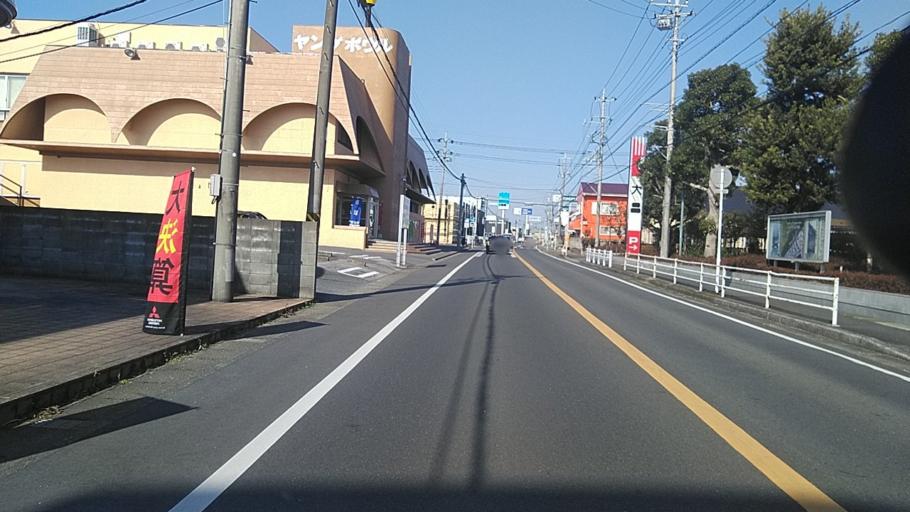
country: JP
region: Chiba
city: Mobara
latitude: 35.4345
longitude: 140.2935
